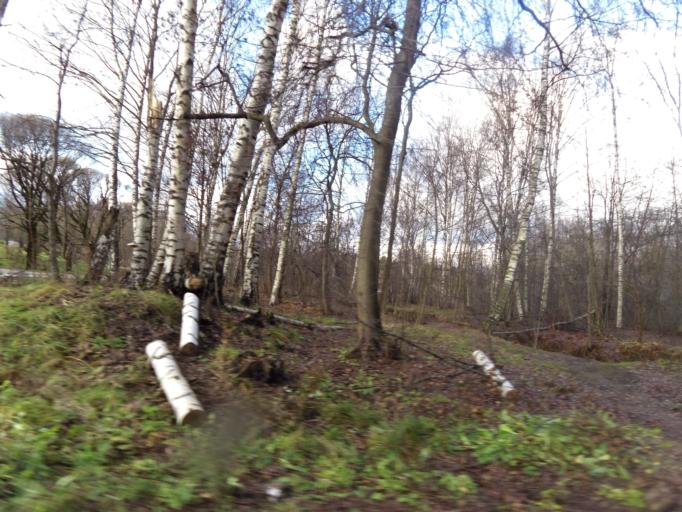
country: FI
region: Uusimaa
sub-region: Helsinki
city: Koukkuniemi
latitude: 60.1853
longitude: 24.7651
